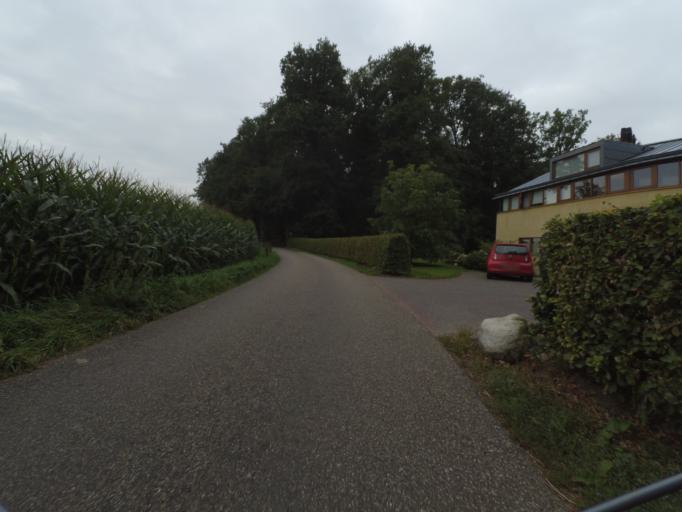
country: NL
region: Overijssel
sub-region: Gemeente Oldenzaal
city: Oldenzaal
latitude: 52.3169
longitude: 6.9661
